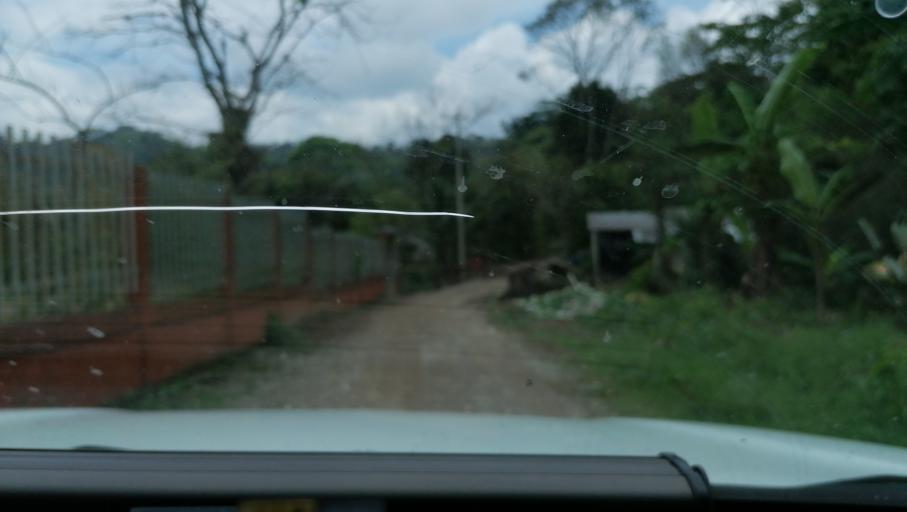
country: MX
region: Chiapas
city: Ocotepec
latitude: 17.3187
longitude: -93.1375
